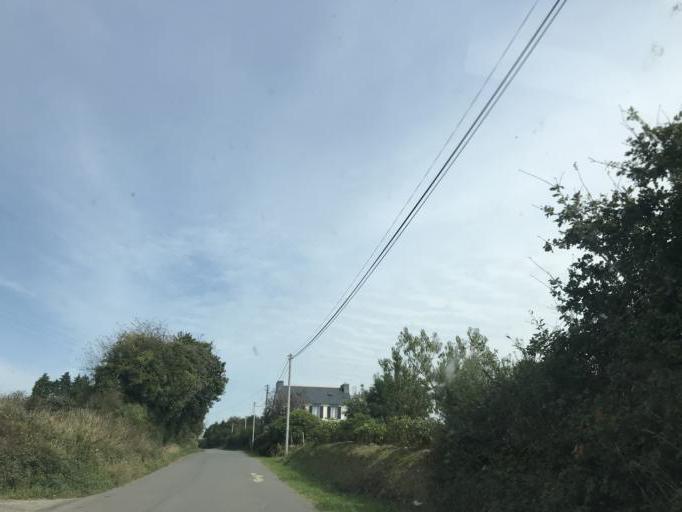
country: FR
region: Brittany
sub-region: Departement du Finistere
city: Brasparts
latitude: 48.3127
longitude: -3.9353
